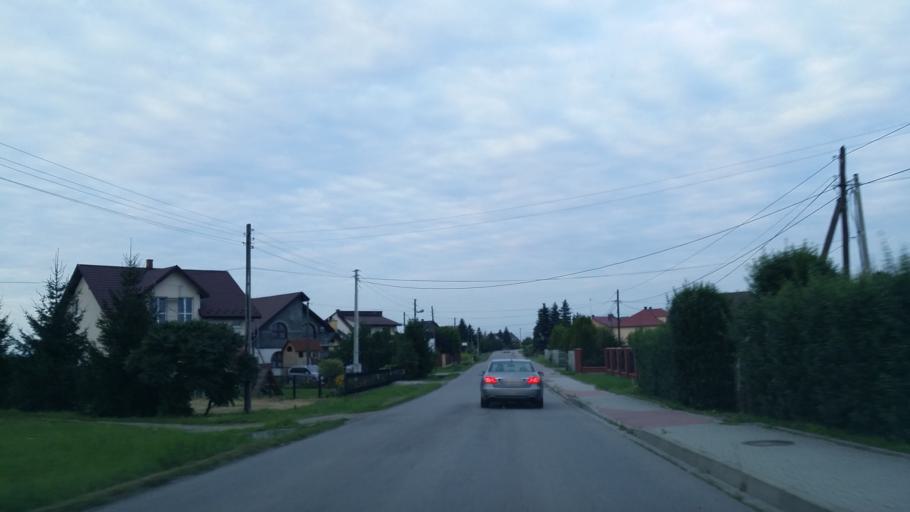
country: PL
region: Lesser Poland Voivodeship
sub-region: Powiat krakowski
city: Kaszow
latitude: 50.0179
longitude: 19.7218
